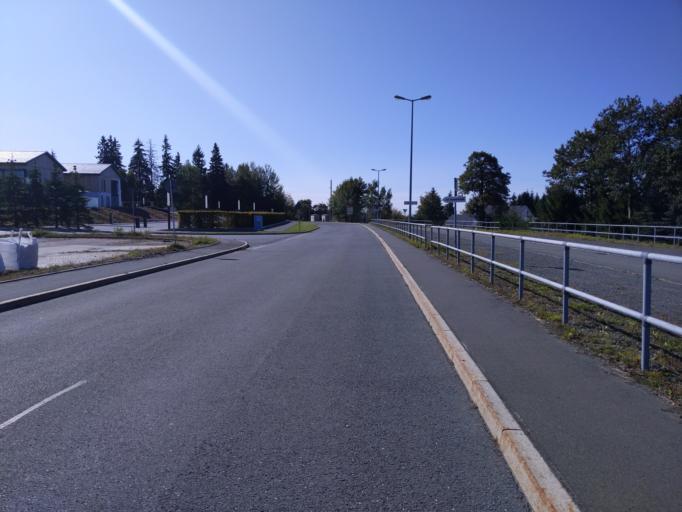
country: DE
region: Saxony
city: Pohl
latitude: 50.3949
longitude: 12.3433
